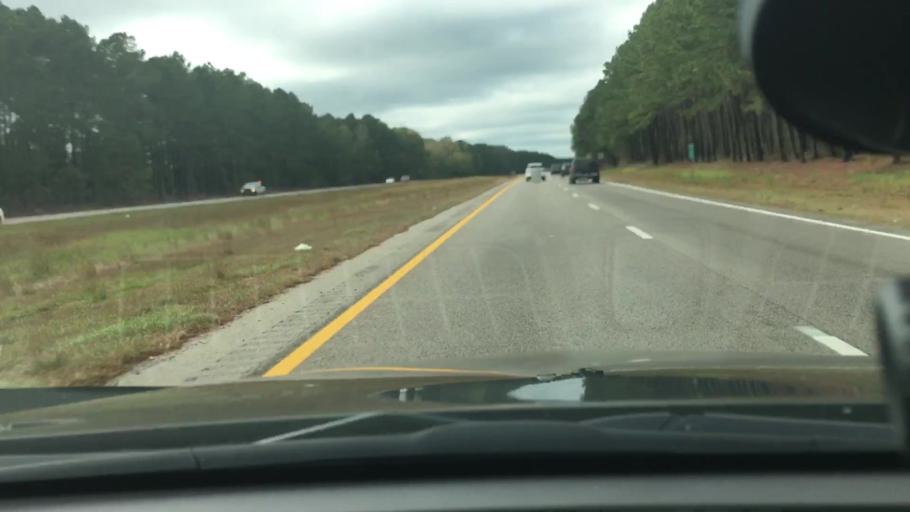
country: US
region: North Carolina
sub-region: Nash County
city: Spring Hope
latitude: 35.7882
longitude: -78.1271
